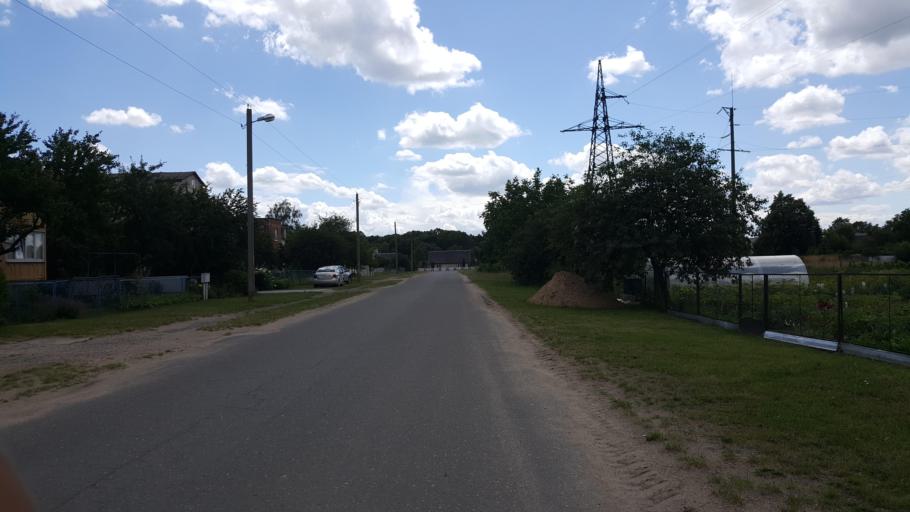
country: BY
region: Brest
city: Kamyanyets
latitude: 52.3195
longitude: 23.9245
